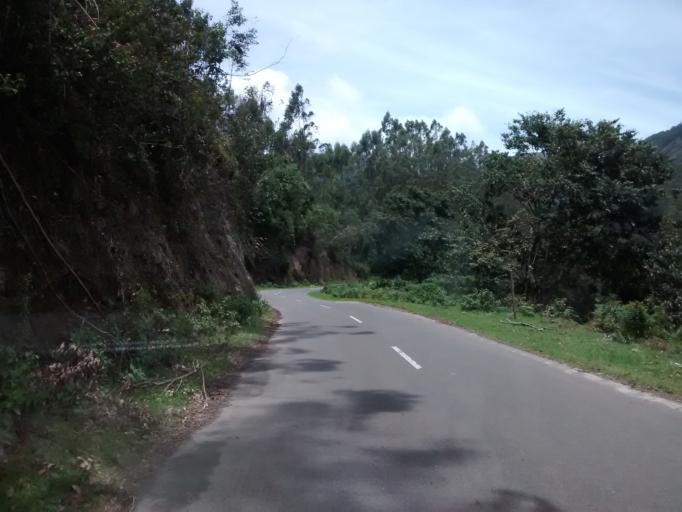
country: IN
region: Kerala
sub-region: Idukki
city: Munnar
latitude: 10.1406
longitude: 77.2056
